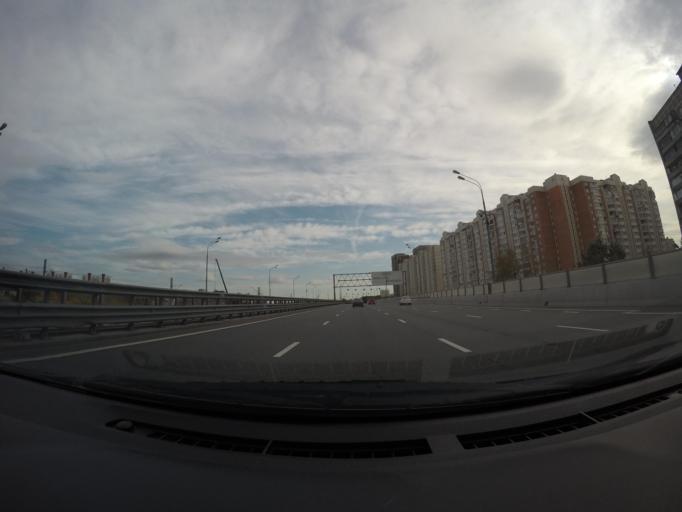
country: RU
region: Moscow
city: Novokhovrino
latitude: 55.8730
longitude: 37.4992
